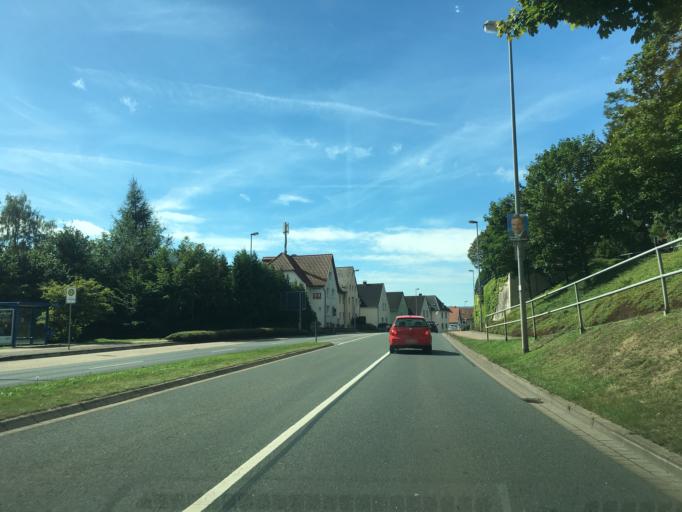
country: DE
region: Lower Saxony
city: Hameln
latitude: 52.0902
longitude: 9.3513
